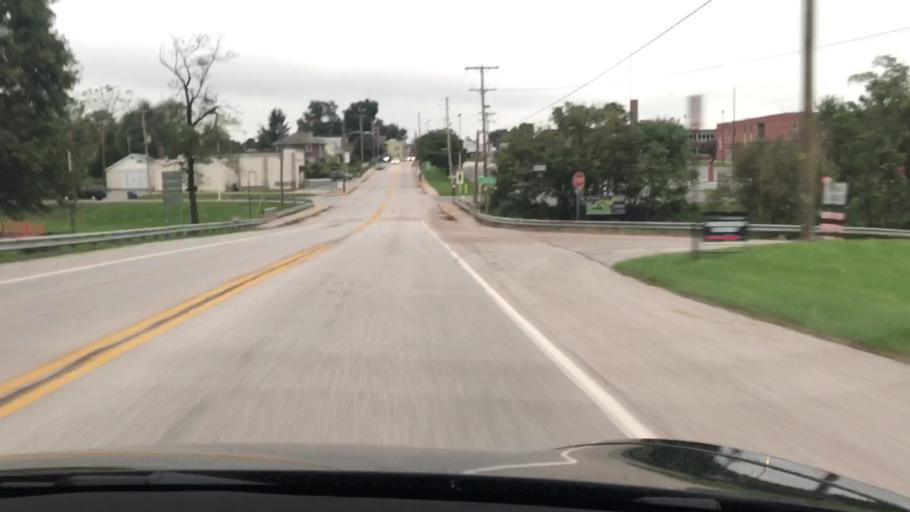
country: US
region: Pennsylvania
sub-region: York County
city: Dover
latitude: 39.9977
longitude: -76.8546
